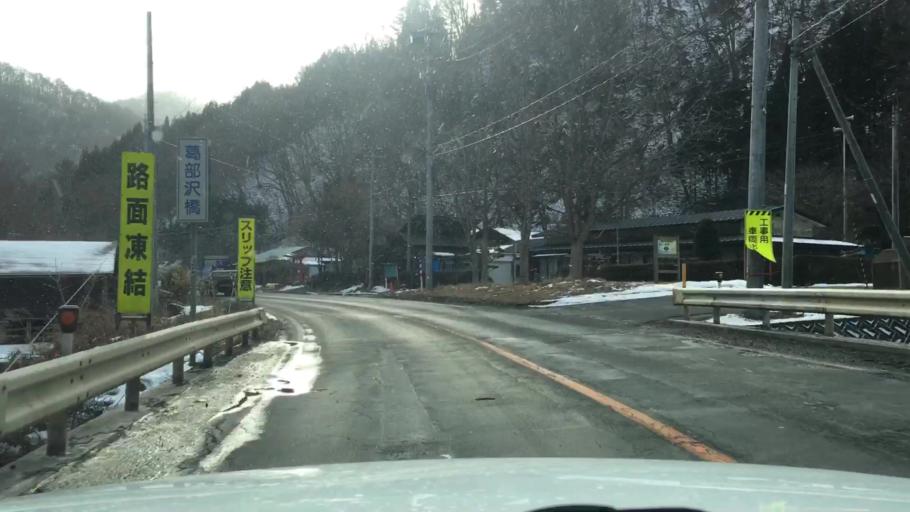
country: JP
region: Iwate
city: Tono
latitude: 39.6270
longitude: 141.5143
